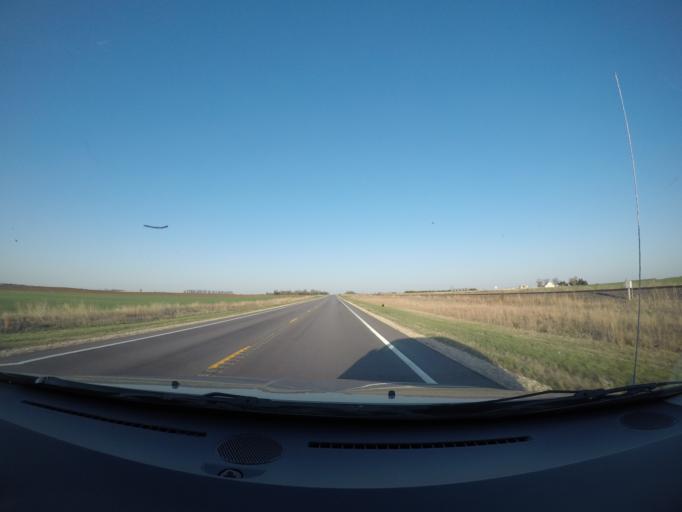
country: US
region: Kansas
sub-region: Stafford County
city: Stafford
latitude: 37.7996
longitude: -98.4577
